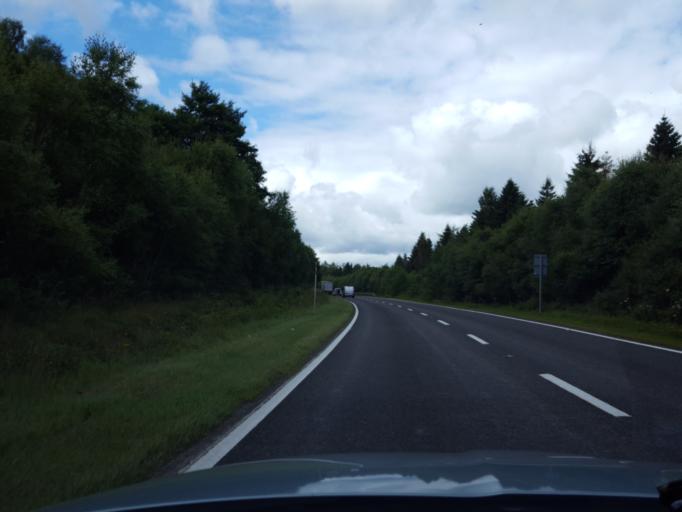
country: GB
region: Scotland
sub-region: Highland
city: Grantown on Spey
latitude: 57.3192
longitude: -3.5832
